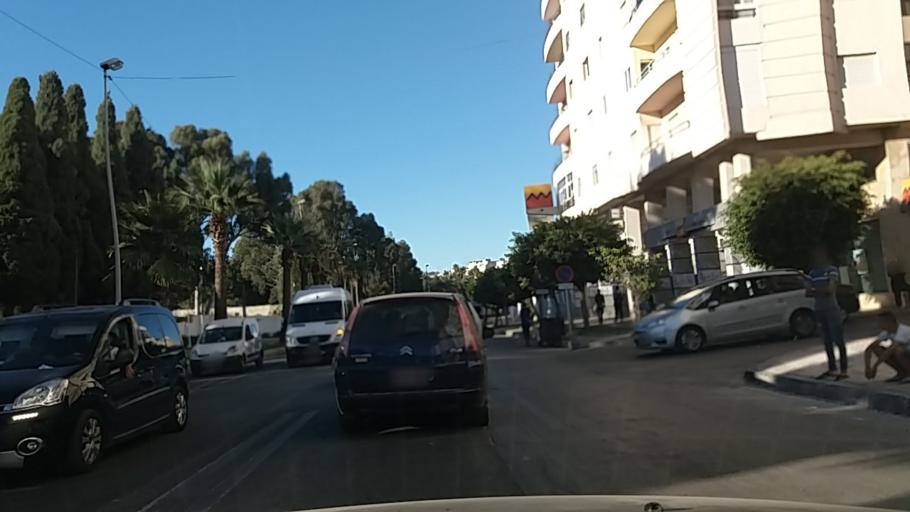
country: MA
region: Tanger-Tetouan
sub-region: Tanger-Assilah
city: Tangier
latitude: 35.7642
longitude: -5.8182
